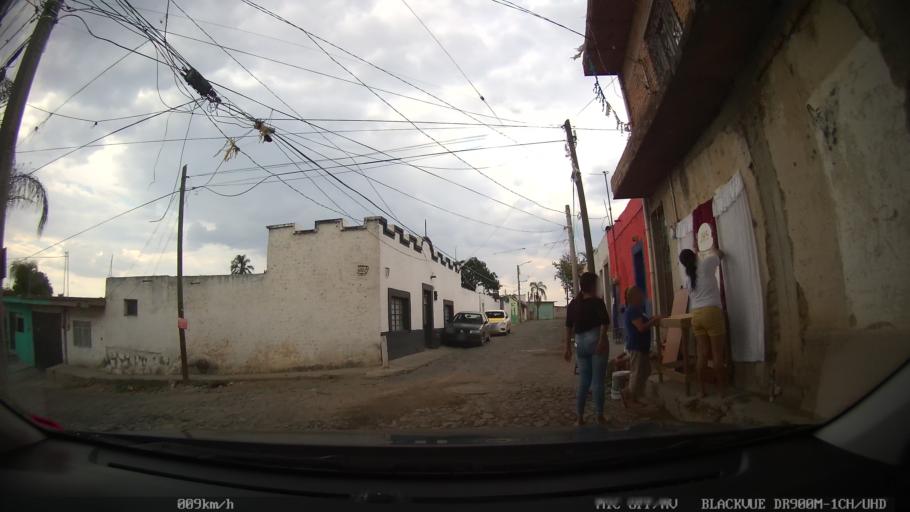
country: MX
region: Jalisco
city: Tlaquepaque
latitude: 20.6202
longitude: -103.2685
